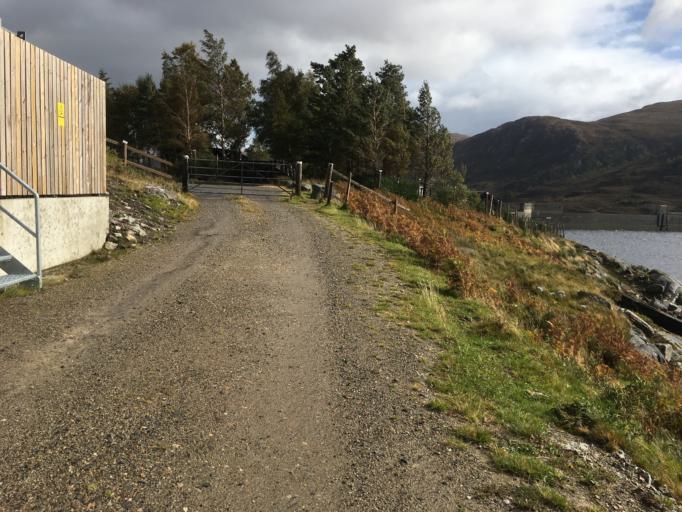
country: GB
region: Scotland
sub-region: Highland
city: Spean Bridge
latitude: 57.3397
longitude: -4.9619
